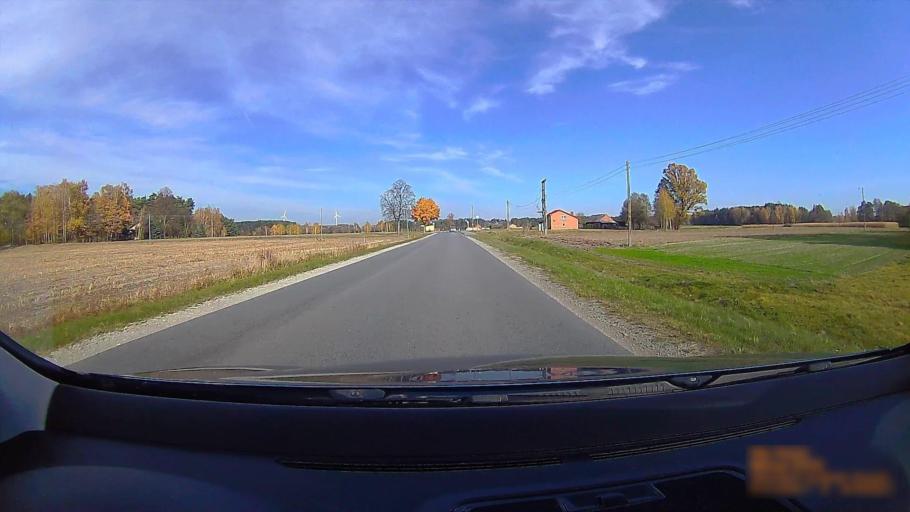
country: PL
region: Greater Poland Voivodeship
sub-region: Powiat ostrzeszowski
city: Doruchow
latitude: 51.3781
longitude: 18.0414
